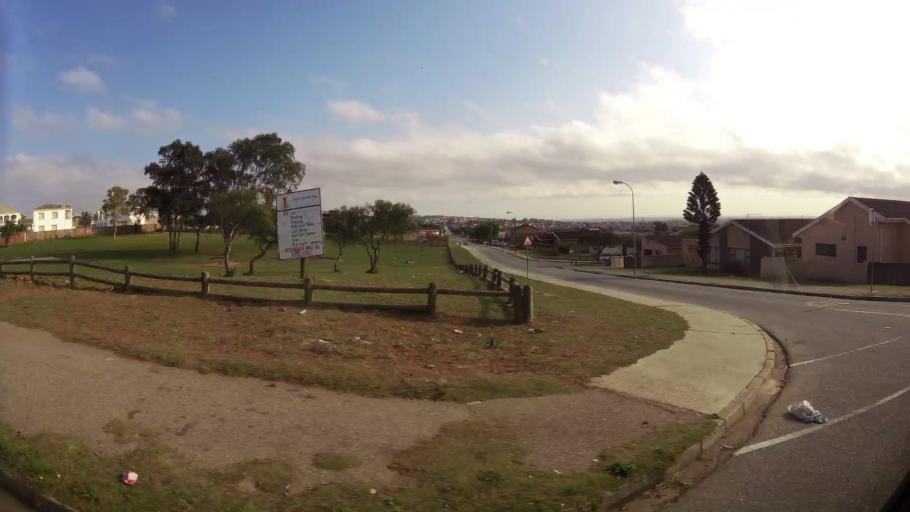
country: ZA
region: Eastern Cape
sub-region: Nelson Mandela Bay Metropolitan Municipality
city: Port Elizabeth
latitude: -33.9245
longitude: 25.5564
